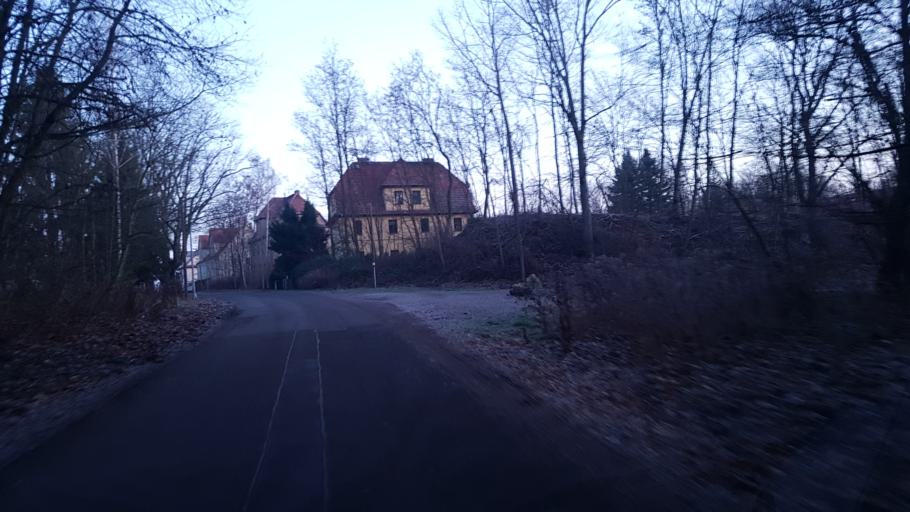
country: DE
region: Brandenburg
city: Schipkau
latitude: 51.5479
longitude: 13.8851
